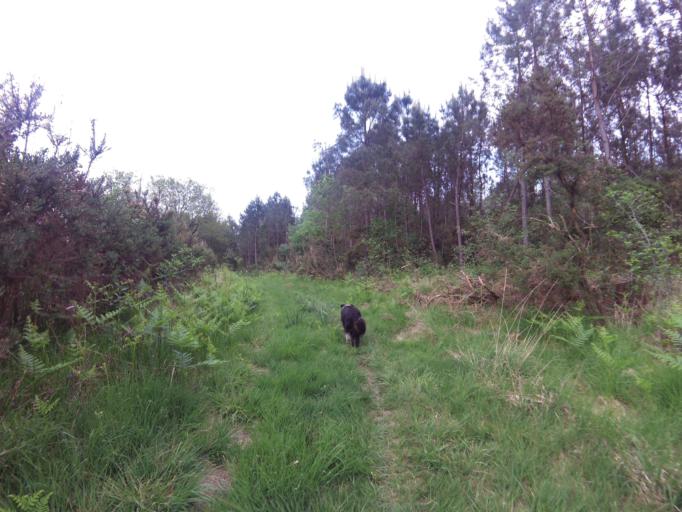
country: FR
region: Brittany
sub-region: Departement du Morbihan
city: Molac
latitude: 47.7578
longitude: -2.4333
